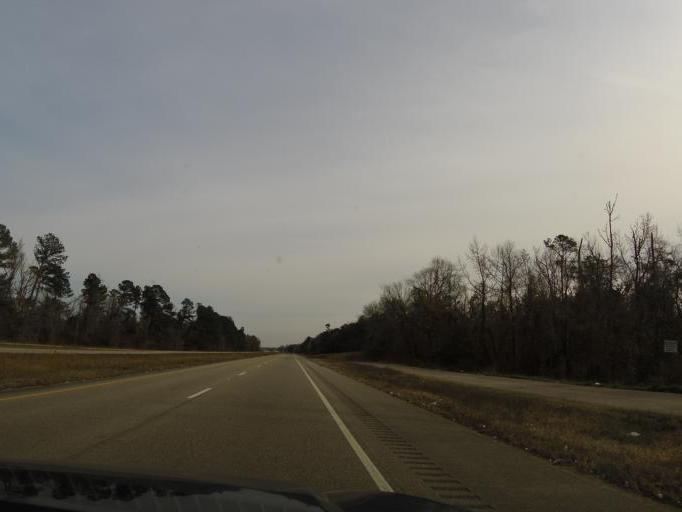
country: US
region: Alabama
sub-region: Houston County
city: Ashford
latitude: 31.1271
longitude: -85.0708
